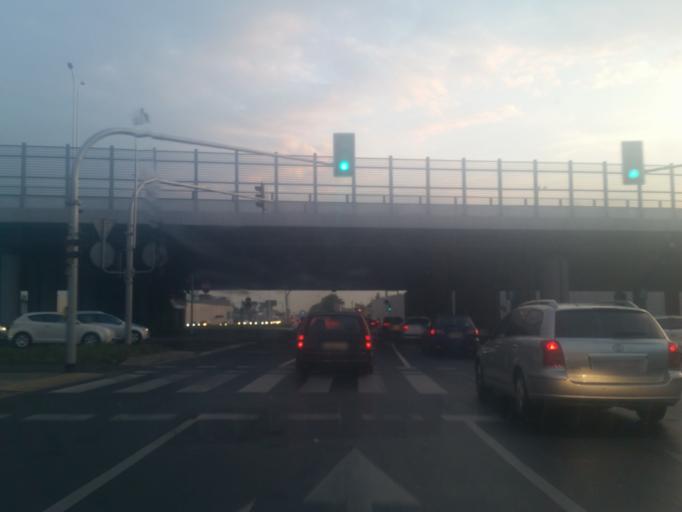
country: PL
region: Masovian Voivodeship
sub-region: Powiat pruszkowski
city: Rybie
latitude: 52.1673
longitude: 20.9341
